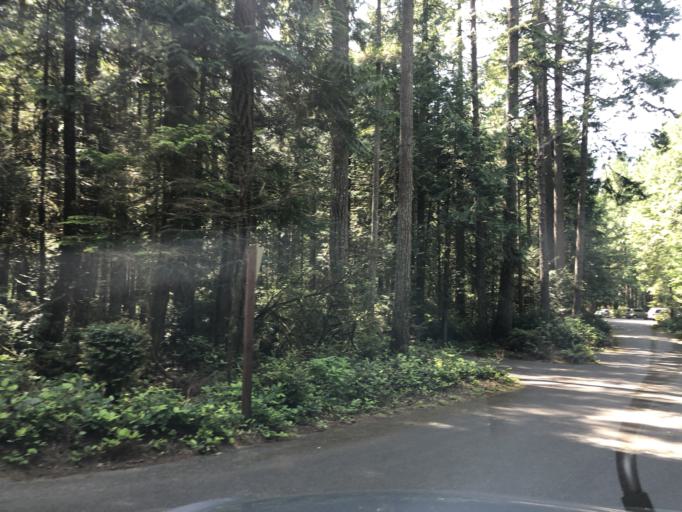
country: US
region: Washington
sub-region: Kitsap County
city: Seabeck
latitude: 47.6487
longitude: -122.8454
